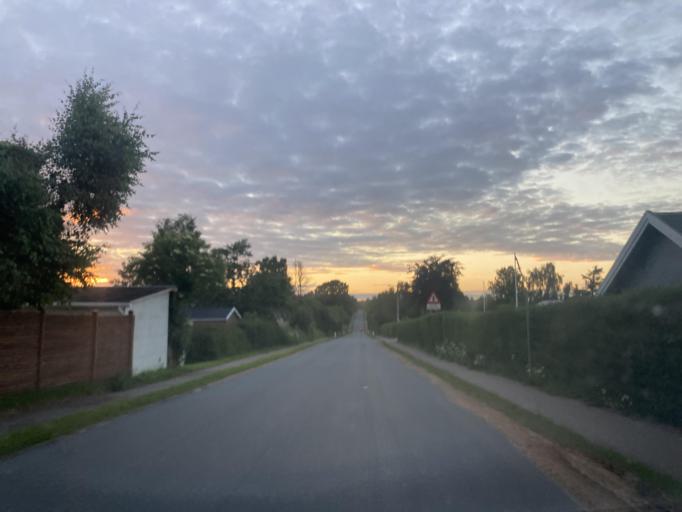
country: DK
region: Capital Region
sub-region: Gribskov Kommune
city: Helsinge
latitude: 56.0628
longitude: 12.1149
